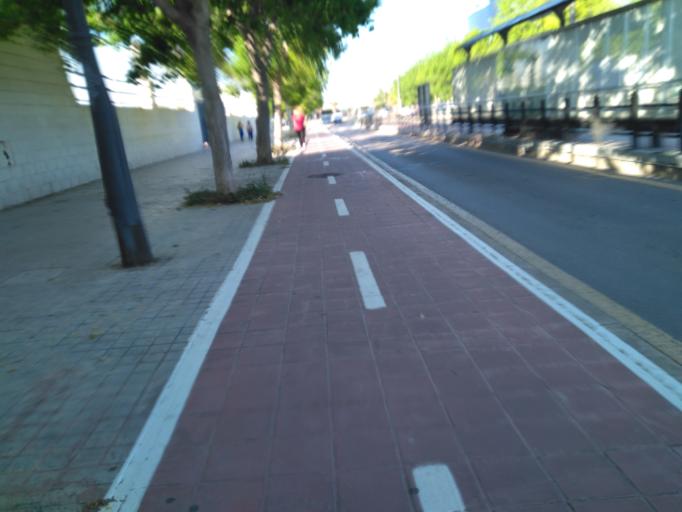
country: ES
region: Valencia
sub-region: Provincia de Valencia
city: Tavernes Blanques
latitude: 39.4950
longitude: -0.3654
